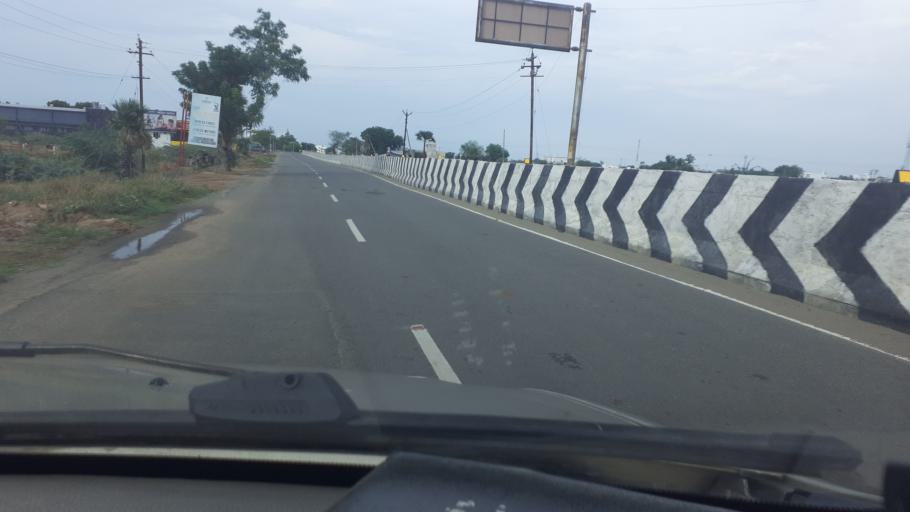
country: IN
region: Tamil Nadu
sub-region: Tirunelveli Kattabo
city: Tirunelveli
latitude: 8.6602
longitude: 77.7147
